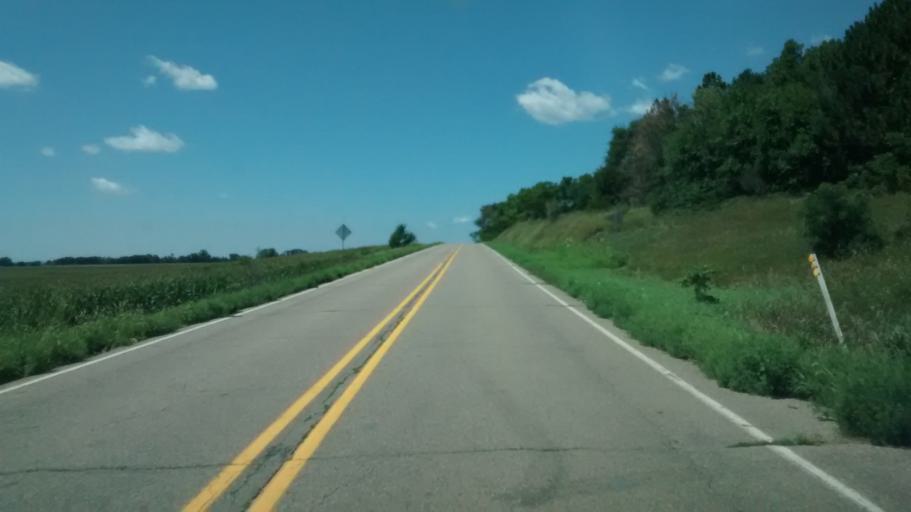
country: US
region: Iowa
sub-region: Woodbury County
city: Moville
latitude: 42.2682
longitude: -96.0641
